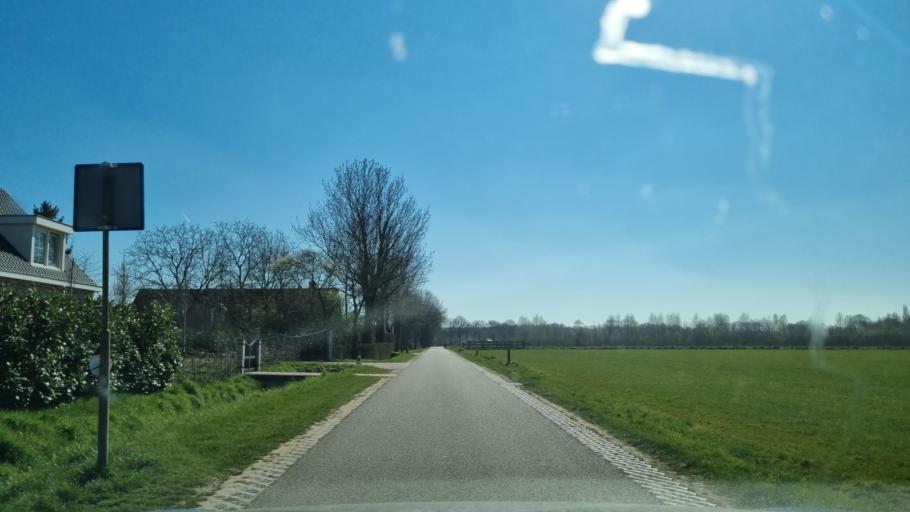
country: NL
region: Gelderland
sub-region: Gemeente Groesbeek
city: De Horst
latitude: 51.7721
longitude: 5.9692
